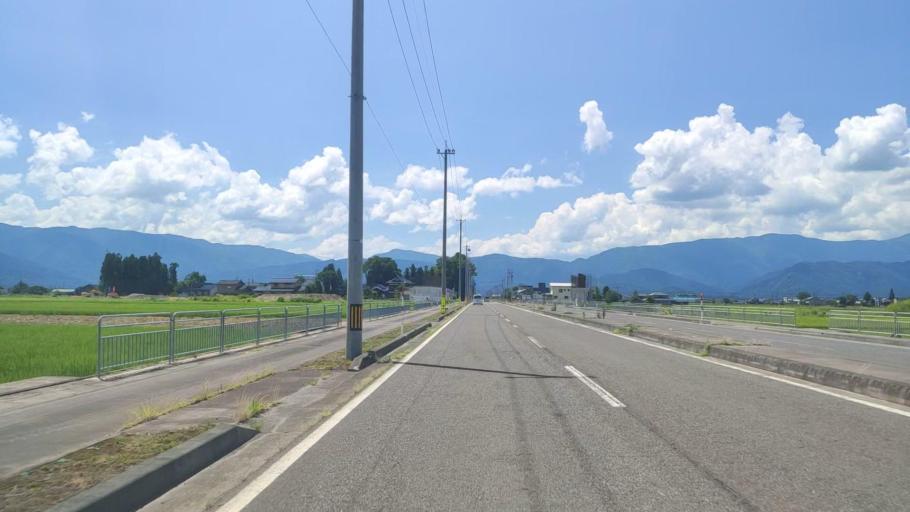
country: JP
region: Fukui
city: Ono
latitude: 35.9994
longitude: 136.5090
